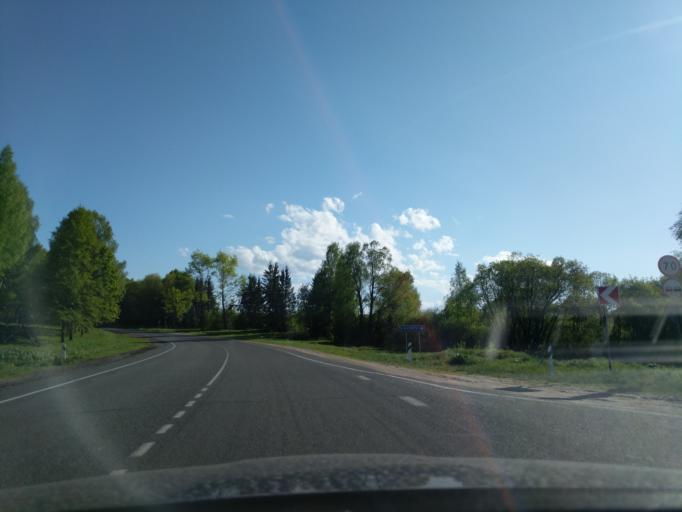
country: BY
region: Minsk
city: Myadzyel
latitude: 54.8577
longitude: 26.9239
